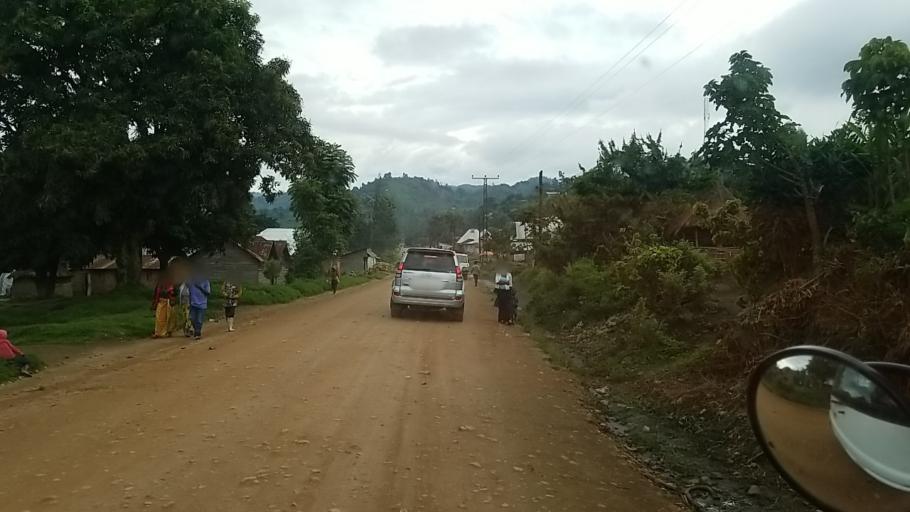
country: CD
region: Nord Kivu
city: Sake
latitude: -1.6929
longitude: 29.0161
